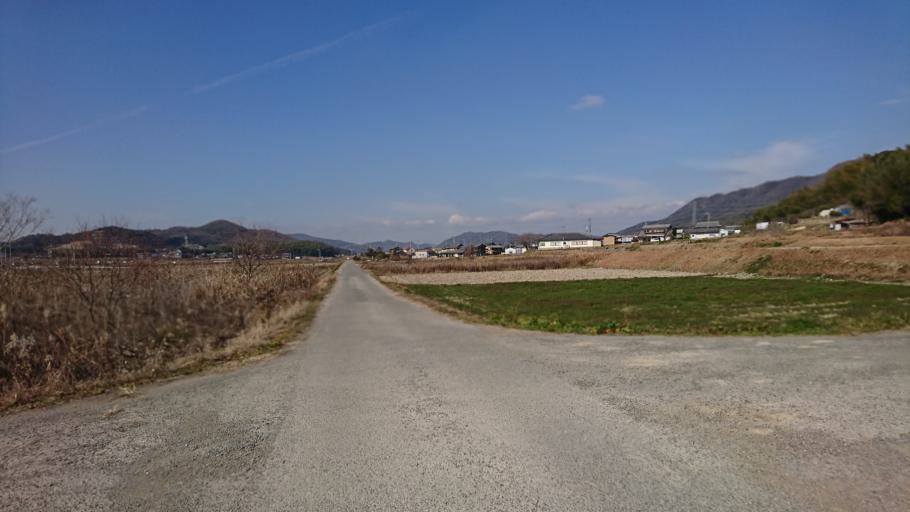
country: JP
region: Hyogo
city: Kakogawacho-honmachi
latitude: 34.8131
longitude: 134.8573
